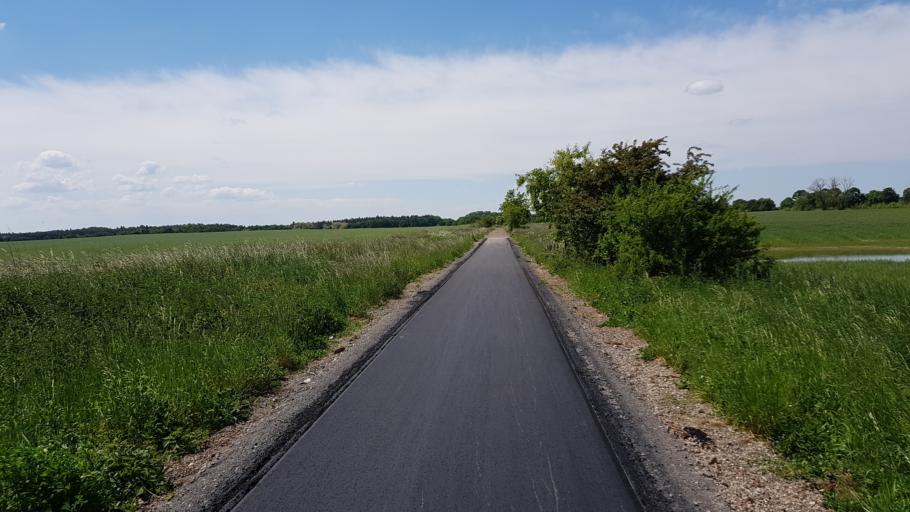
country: PL
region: West Pomeranian Voivodeship
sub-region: Powiat mysliborski
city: Barlinek
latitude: 52.9877
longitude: 15.1452
